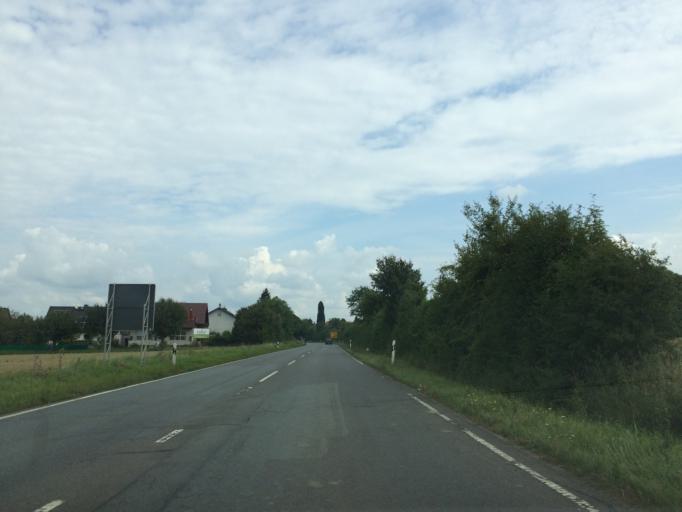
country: DE
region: Hesse
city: Gross-Umstadt
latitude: 49.8897
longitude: 8.9367
